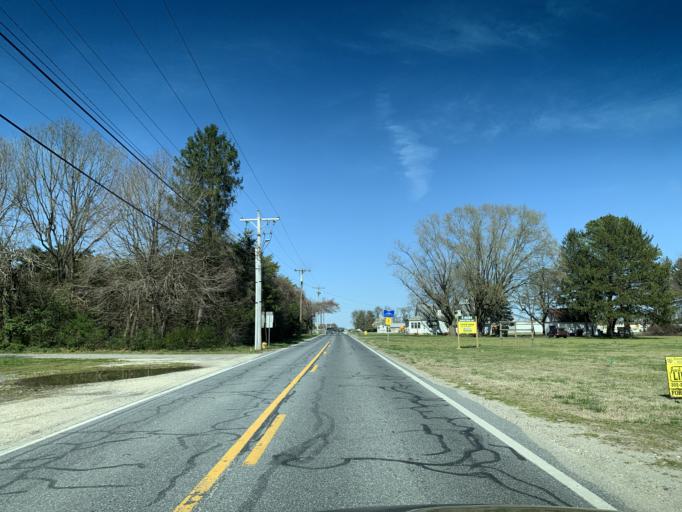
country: US
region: Delaware
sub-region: Sussex County
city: Milford
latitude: 38.9198
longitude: -75.4183
